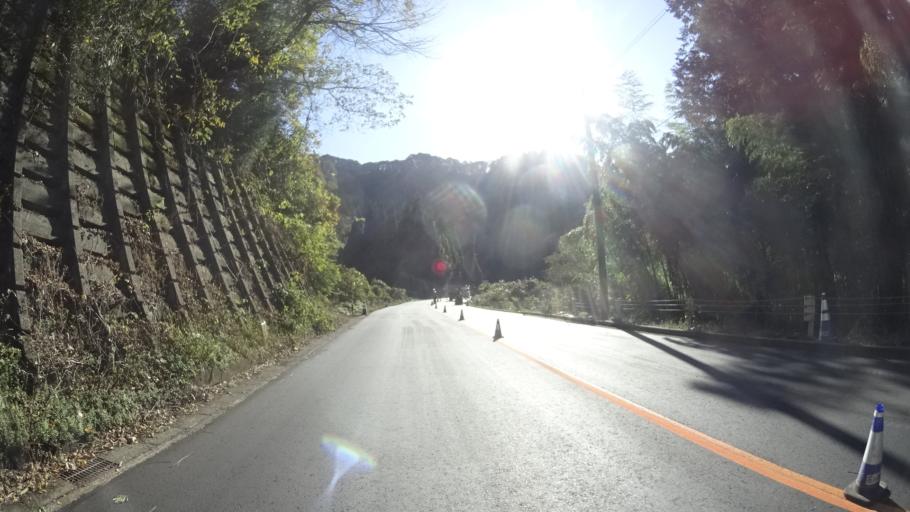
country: JP
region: Ishikawa
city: Tsurugi-asahimachi
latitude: 36.3717
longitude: 136.5819
